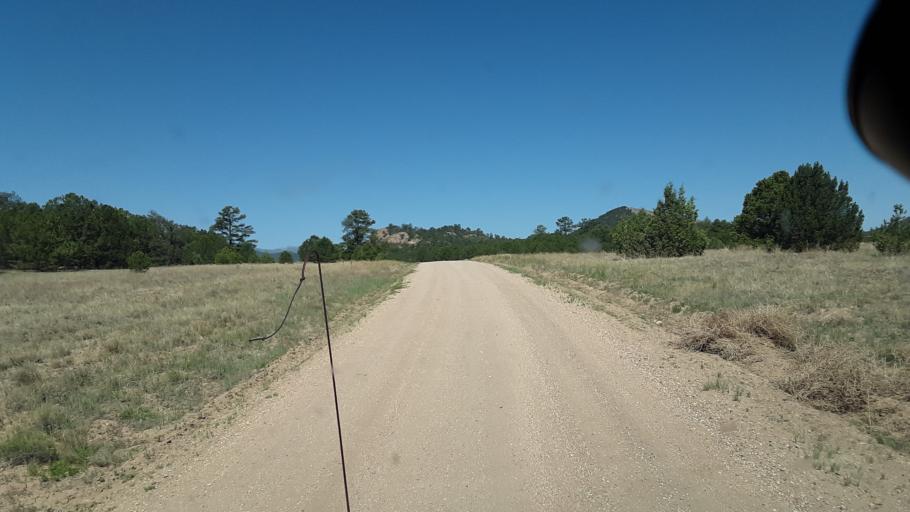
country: US
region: Colorado
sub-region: Custer County
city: Westcliffe
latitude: 38.2950
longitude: -105.4715
